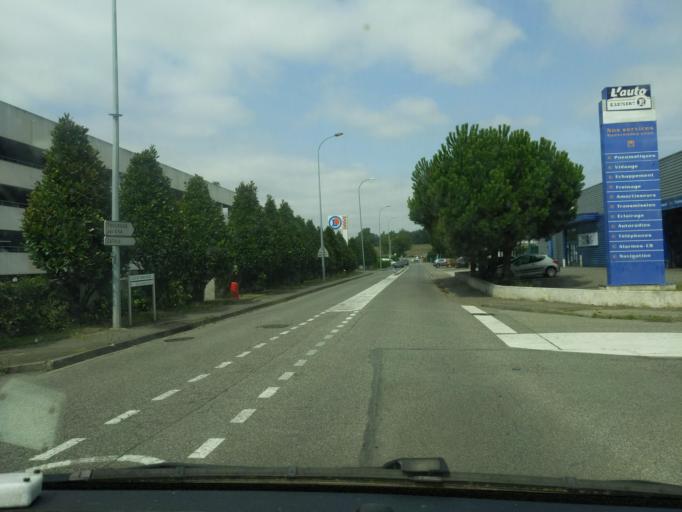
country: FR
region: Midi-Pyrenees
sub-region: Departement de la Haute-Garonne
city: Saint-Orens-de-Gameville
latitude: 43.5659
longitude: 1.5196
